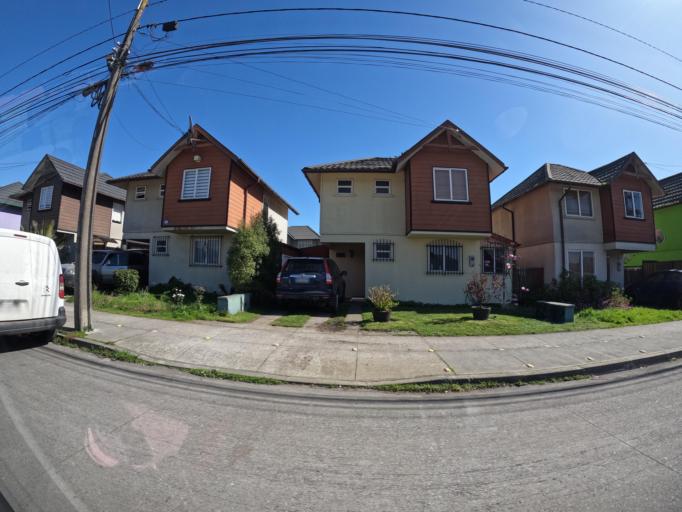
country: CL
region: Biobio
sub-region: Provincia de Concepcion
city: Concepcion
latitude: -36.8844
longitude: -73.1456
